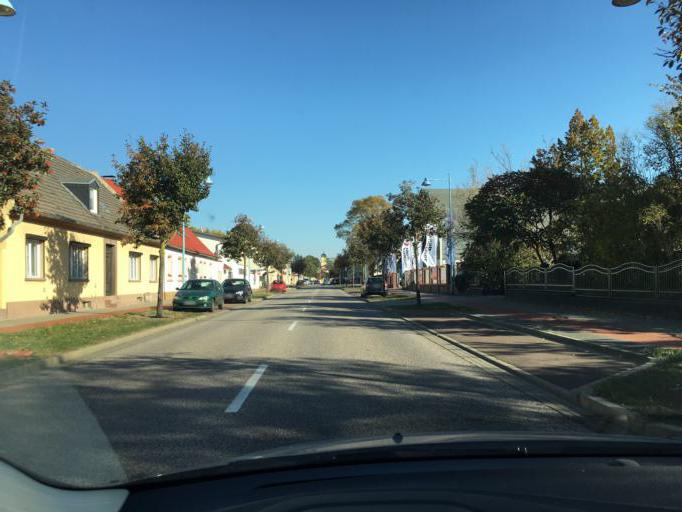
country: DE
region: Saxony-Anhalt
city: Bernburg
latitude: 51.7991
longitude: 11.7667
